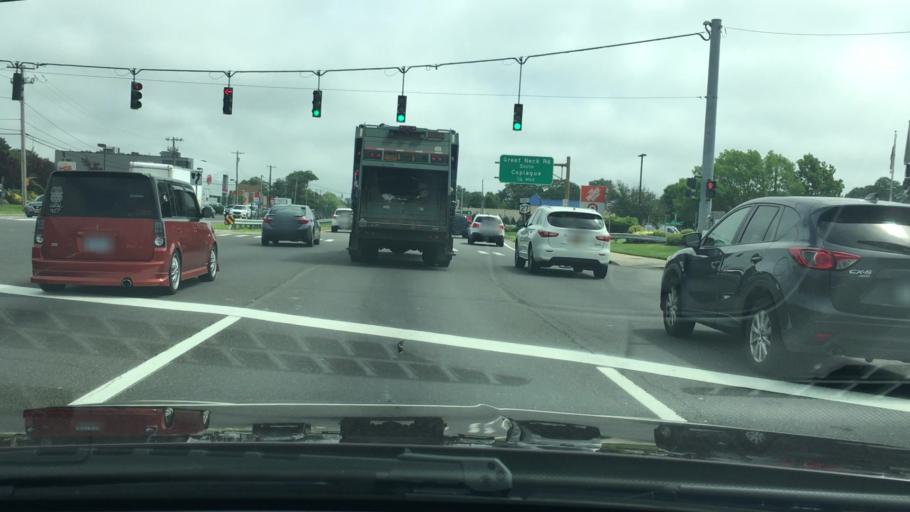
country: US
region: New York
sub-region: Suffolk County
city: Copiague
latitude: 40.6890
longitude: -73.4089
